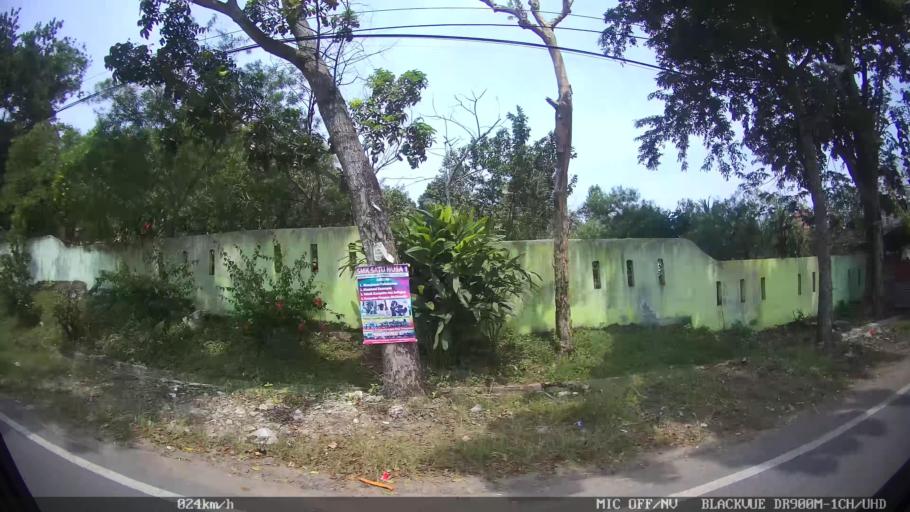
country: ID
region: Lampung
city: Bandarlampung
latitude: -5.4545
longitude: 105.2477
